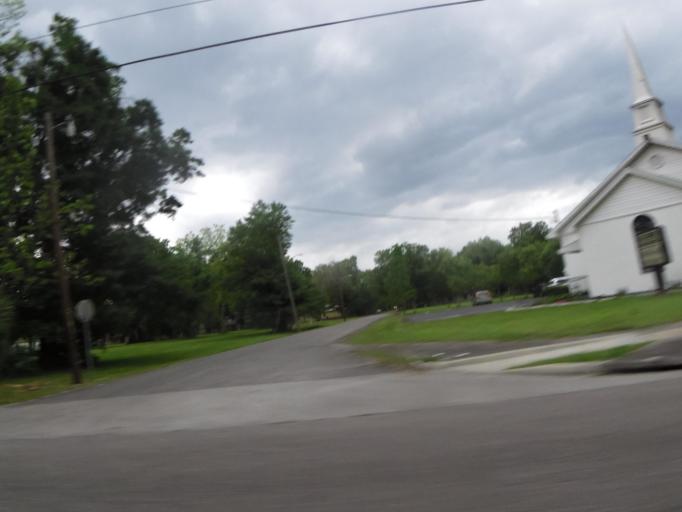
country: US
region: Florida
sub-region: Duval County
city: Jacksonville
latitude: 30.3352
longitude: -81.7226
